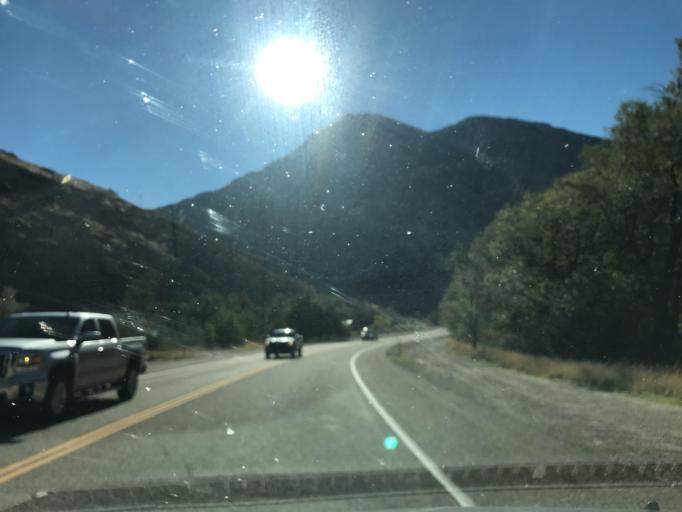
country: US
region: Utah
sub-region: Weber County
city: Ogden
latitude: 41.2386
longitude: -111.9308
